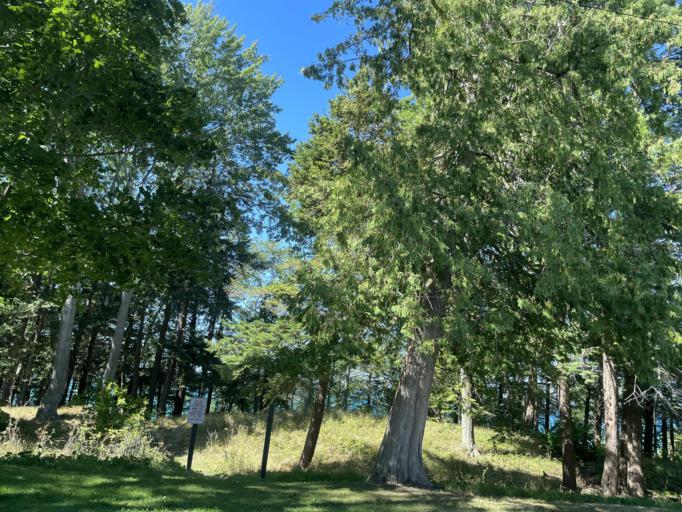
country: US
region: Michigan
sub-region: Charlevoix County
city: Charlevoix
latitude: 45.3165
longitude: -85.2679
